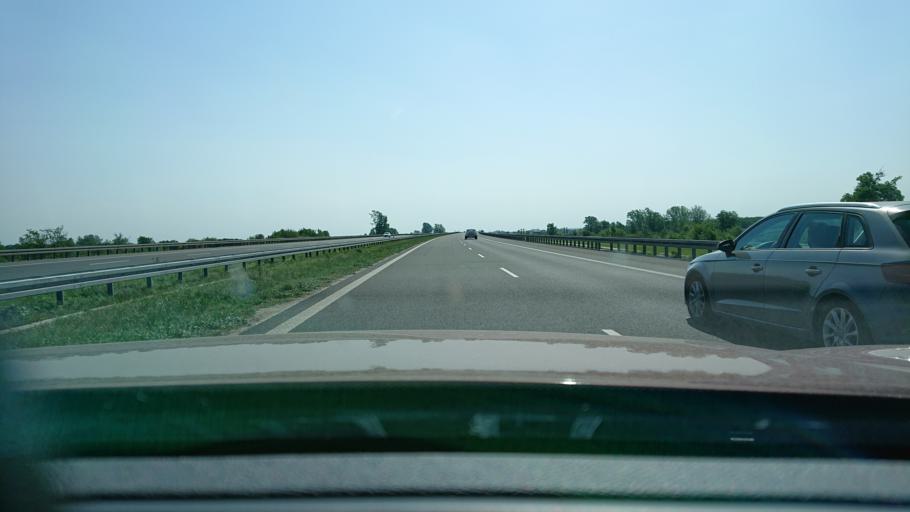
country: PL
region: Subcarpathian Voivodeship
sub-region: Powiat przeworski
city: Grzeska
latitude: 50.1104
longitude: 22.4306
